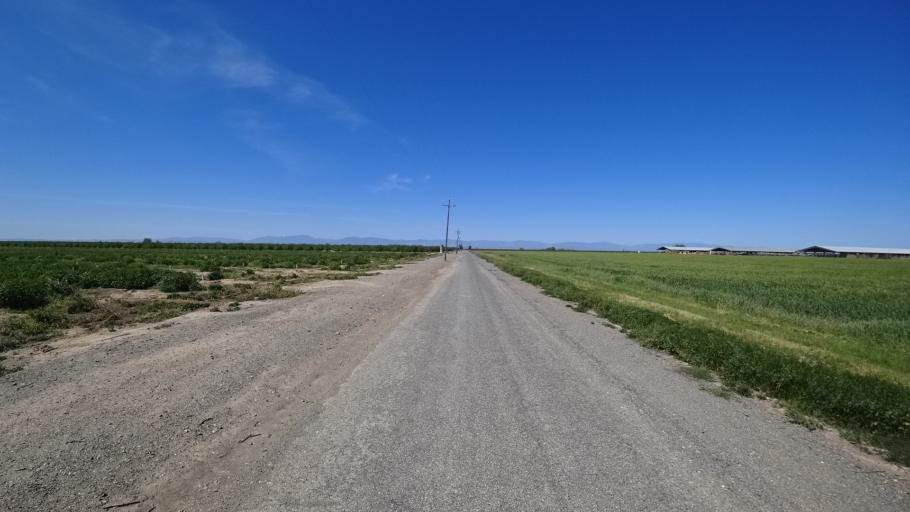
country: US
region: California
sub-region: Glenn County
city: Orland
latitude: 39.6382
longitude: -122.1256
